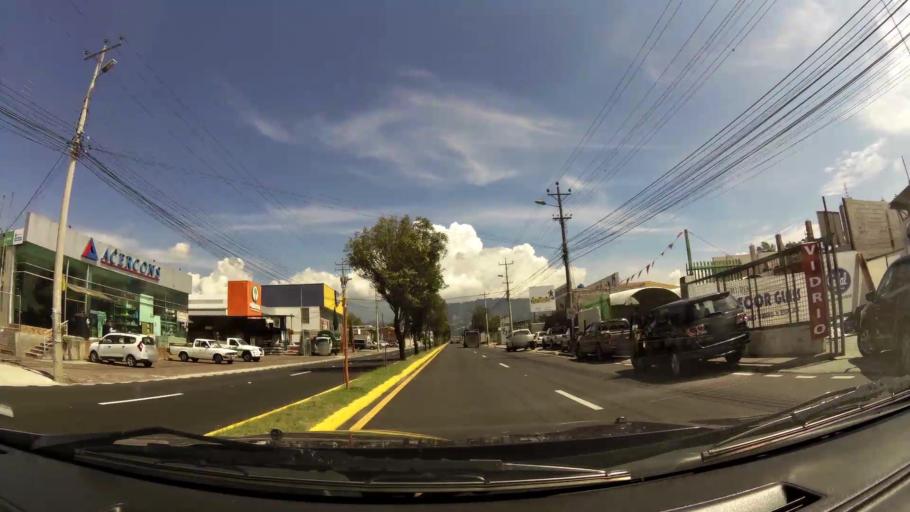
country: EC
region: Pichincha
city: Quito
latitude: -0.2124
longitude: -78.4116
